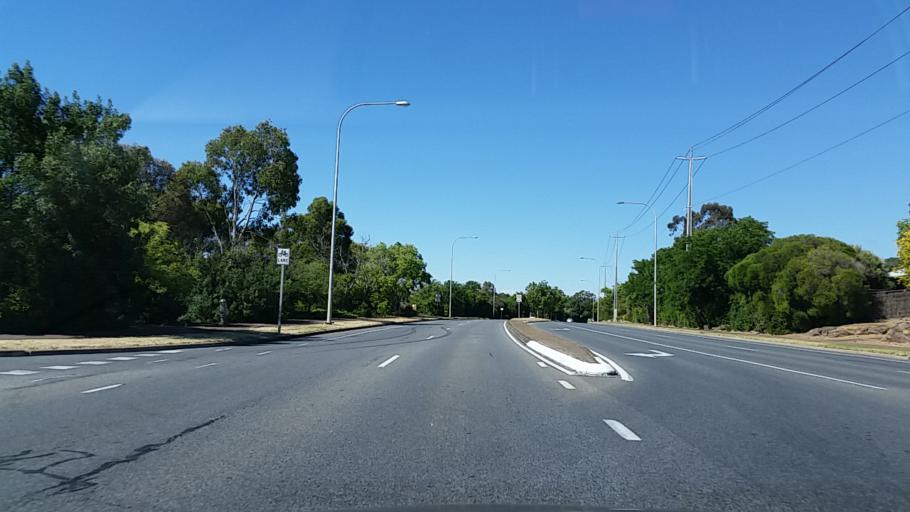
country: AU
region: South Australia
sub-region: Tea Tree Gully
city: Modbury
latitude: -34.7975
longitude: 138.6866
